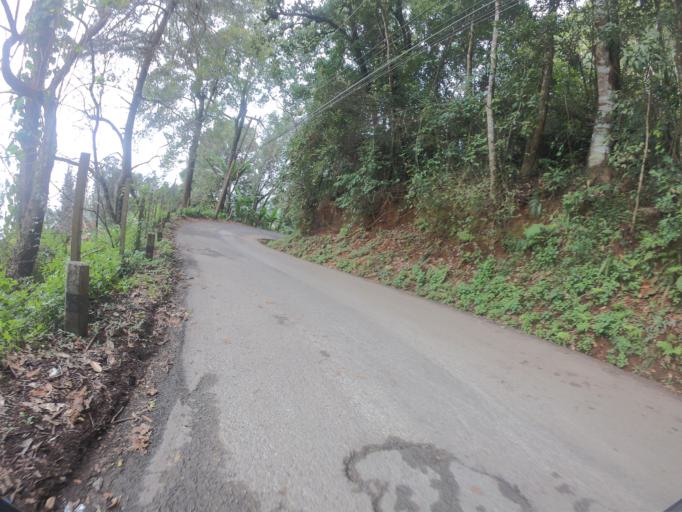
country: TH
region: Chiang Mai
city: Chiang Mai
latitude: 18.8112
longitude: 98.8863
